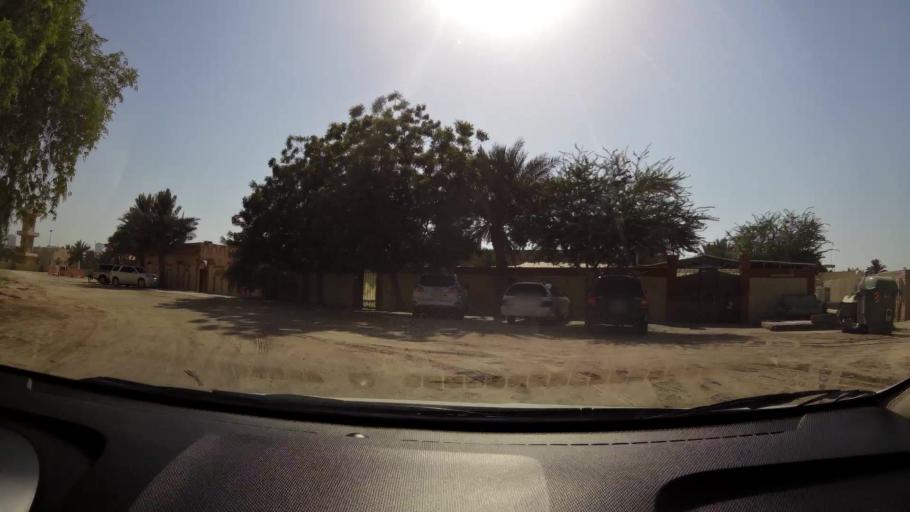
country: AE
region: Ajman
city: Ajman
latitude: 25.4102
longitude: 55.4683
